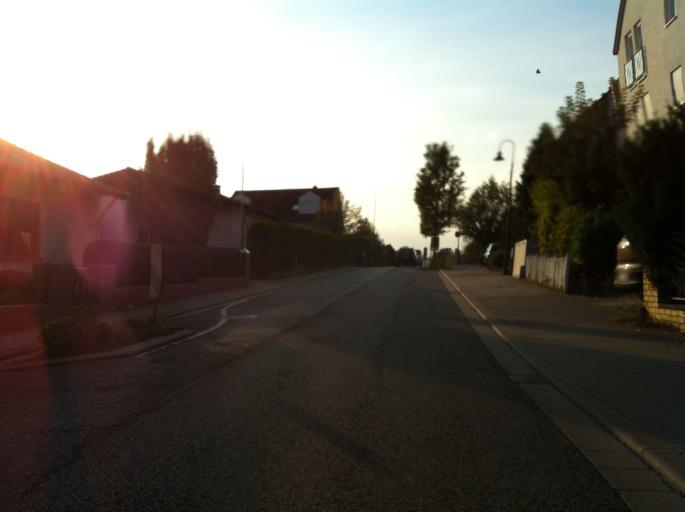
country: DE
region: Rheinland-Pfalz
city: Stadecken-Elsheim
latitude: 49.9173
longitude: 8.1210
